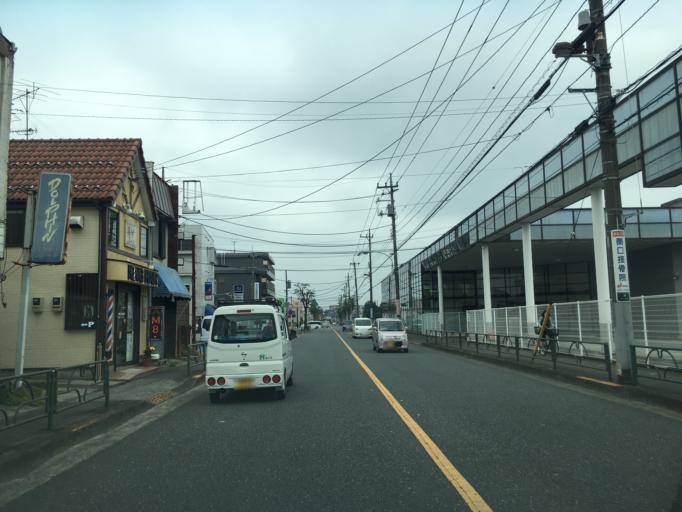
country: JP
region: Tokyo
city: Hino
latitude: 35.7395
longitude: 139.3942
